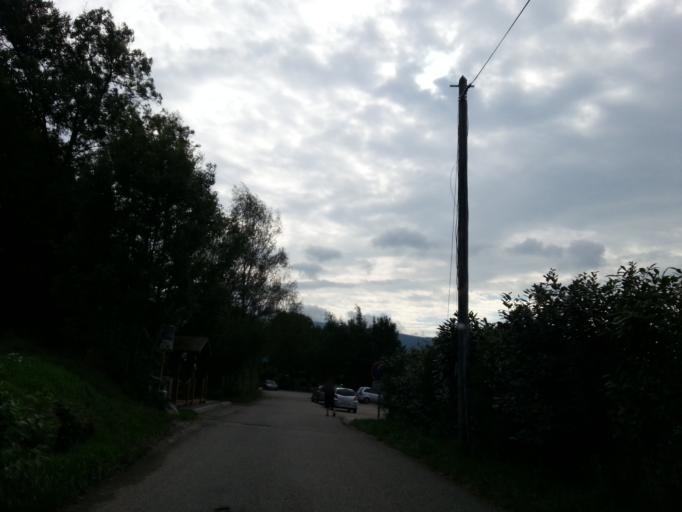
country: FR
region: Rhone-Alpes
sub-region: Departement de la Haute-Savoie
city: Menthon-Saint-Bernard
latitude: 45.8510
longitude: 6.2044
